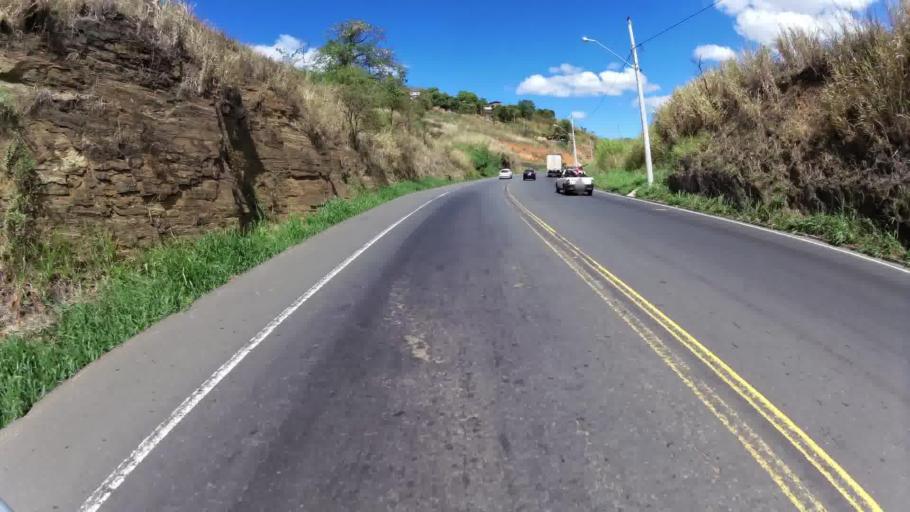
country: BR
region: Minas Gerais
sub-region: Alem Paraiba
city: Alem Paraiba
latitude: -21.8617
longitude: -42.6678
